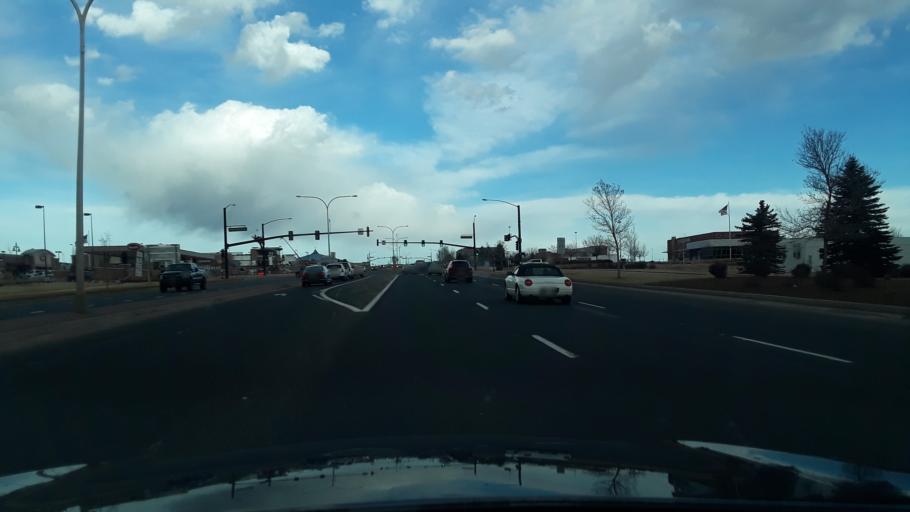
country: US
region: Colorado
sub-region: El Paso County
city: Air Force Academy
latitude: 38.9909
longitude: -104.8092
